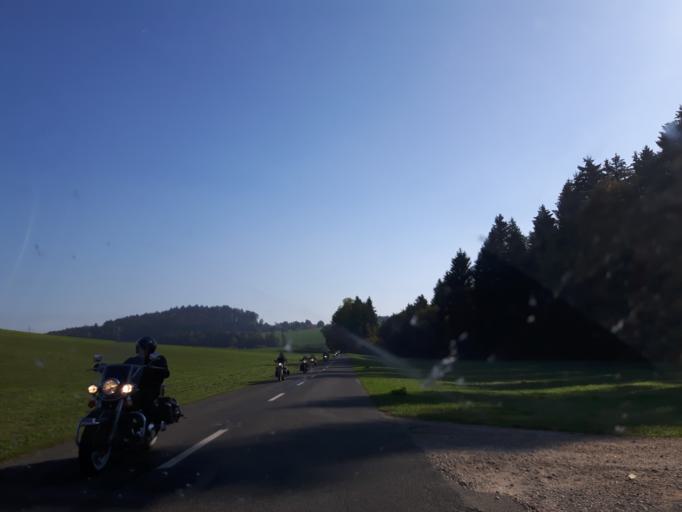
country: CH
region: Lucerne
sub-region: Willisau District
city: Pfaffnau
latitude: 47.2439
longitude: 7.8841
